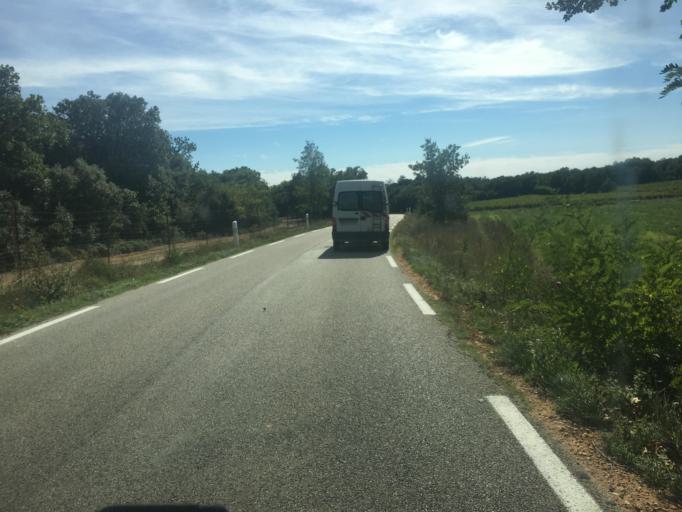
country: FR
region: Languedoc-Roussillon
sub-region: Departement du Gard
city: Connaux
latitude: 44.0498
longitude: 4.5680
